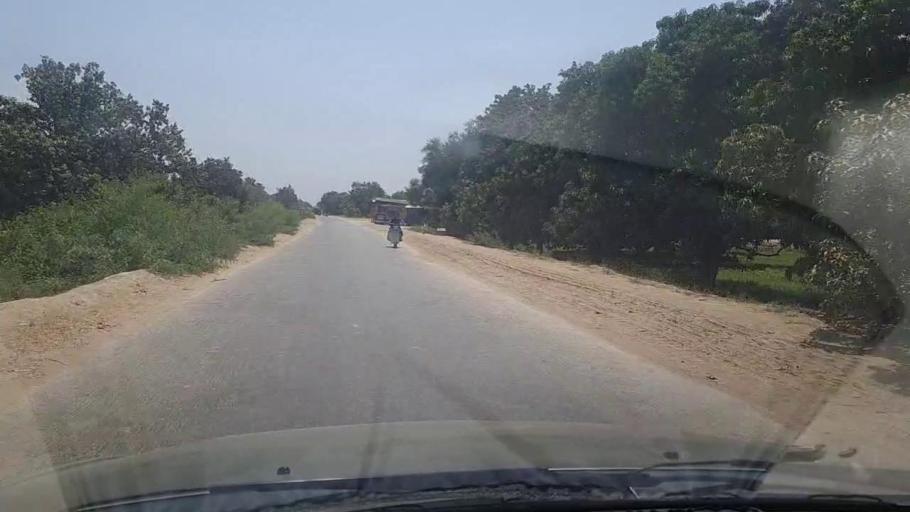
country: PK
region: Sindh
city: Tando Jam
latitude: 25.2869
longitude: 68.5943
